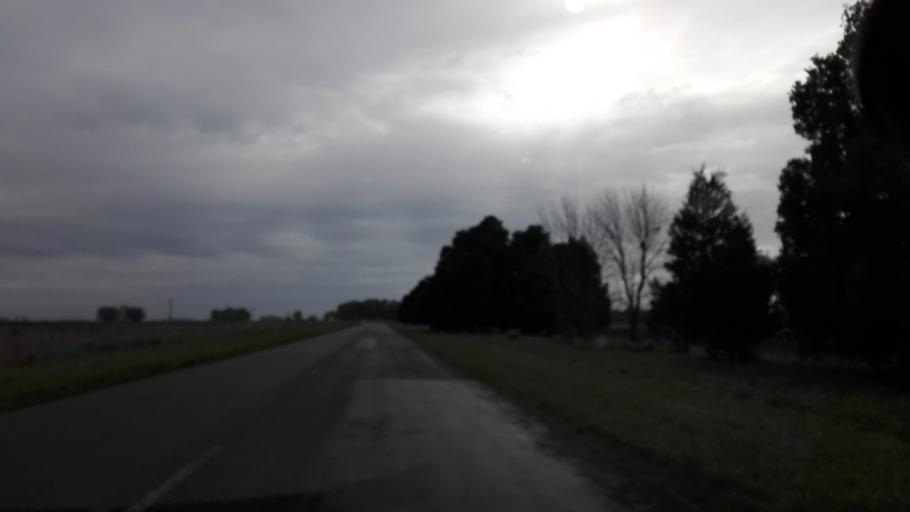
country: AR
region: Buenos Aires
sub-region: Partido de Rauch
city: Rauch
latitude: -36.6742
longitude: -59.0642
